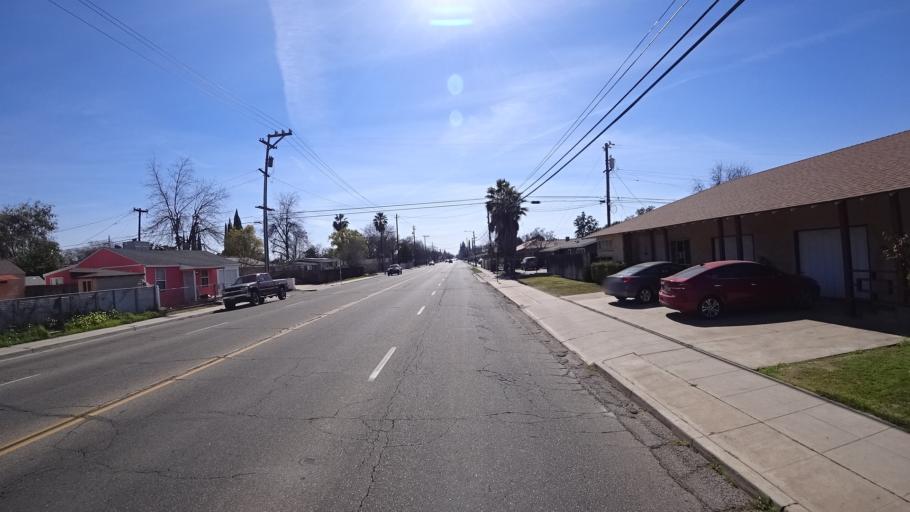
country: US
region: California
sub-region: Fresno County
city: Fresno
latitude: 36.7839
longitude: -119.8087
